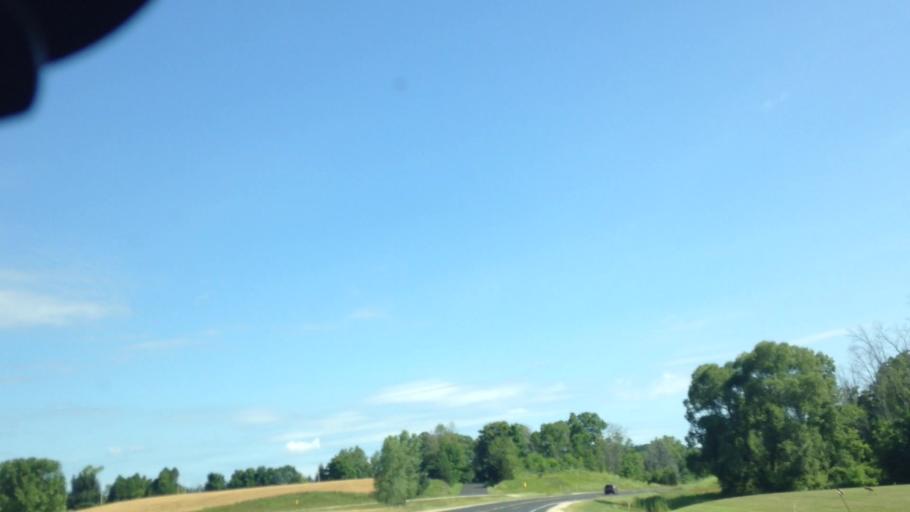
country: US
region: Wisconsin
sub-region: Washington County
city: Slinger
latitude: 43.3631
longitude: -88.2609
